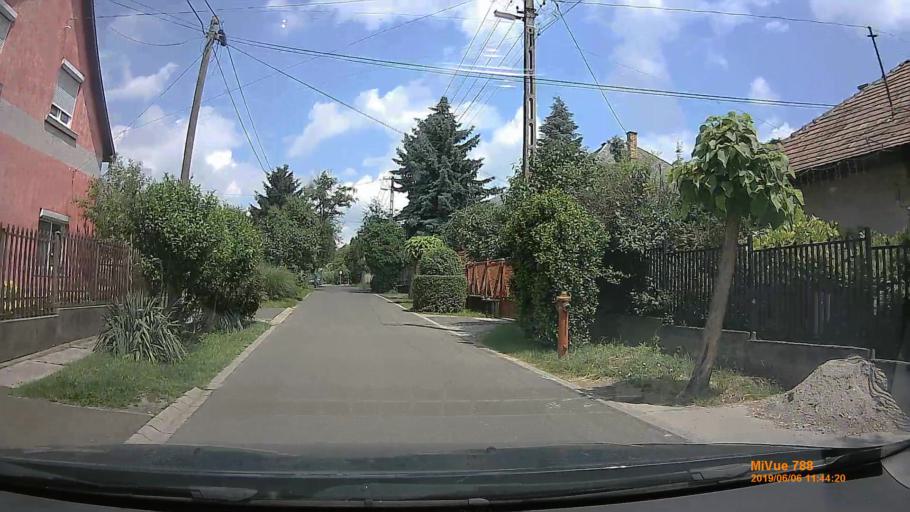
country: HU
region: Pest
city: Maglod
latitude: 47.4437
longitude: 19.3551
